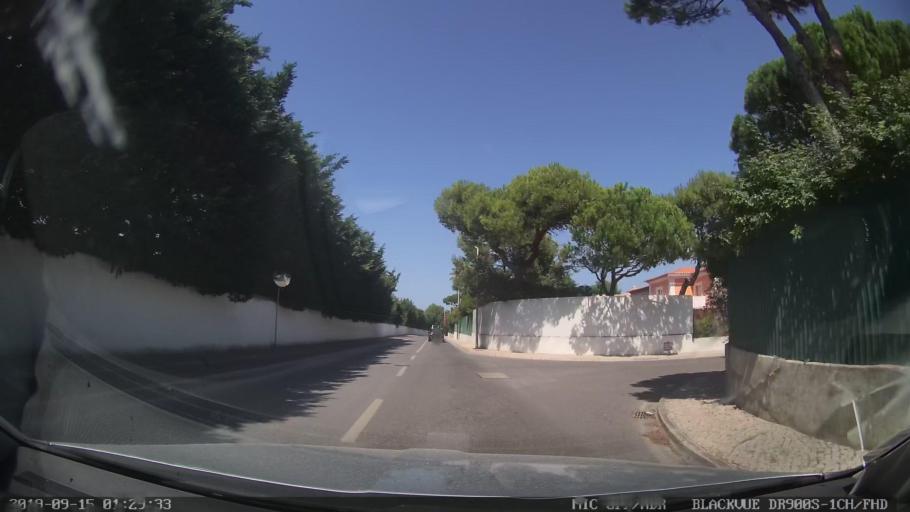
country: PT
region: Lisbon
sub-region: Cascais
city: Cascais
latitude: 38.7192
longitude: -9.4647
